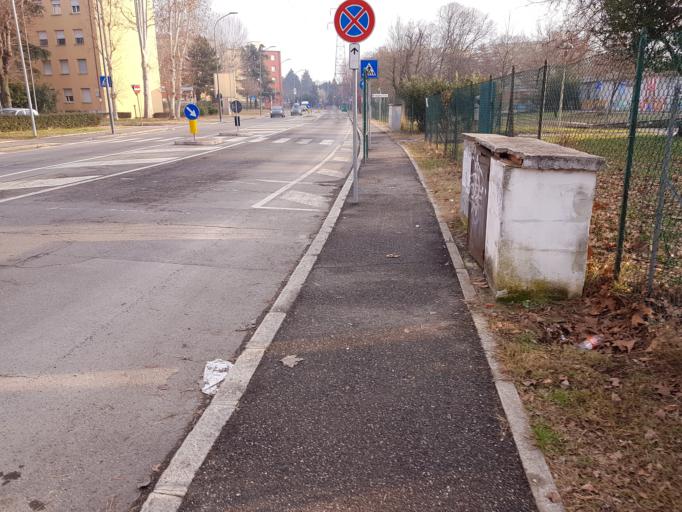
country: IT
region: Emilia-Romagna
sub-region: Provincia di Bologna
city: Quarto Inferiore
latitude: 44.5101
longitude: 11.3927
